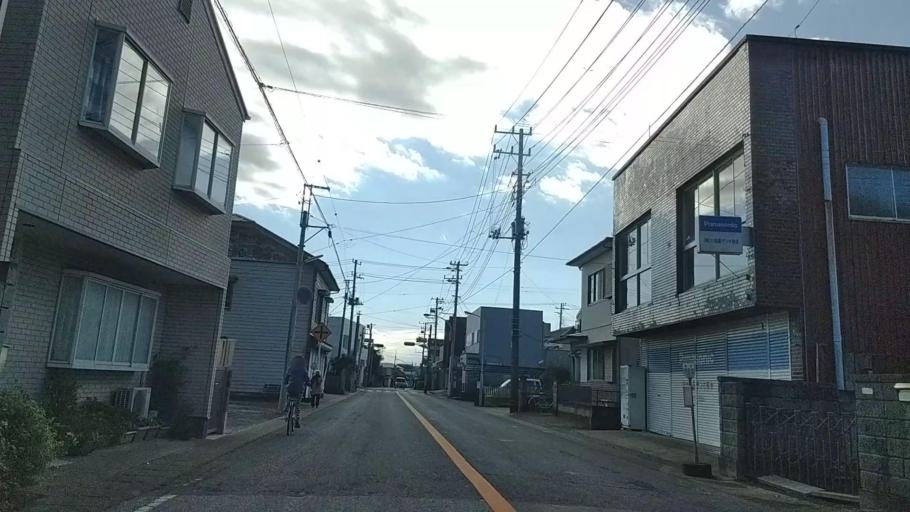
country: JP
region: Chiba
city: Tateyama
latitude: 35.0247
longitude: 139.8592
